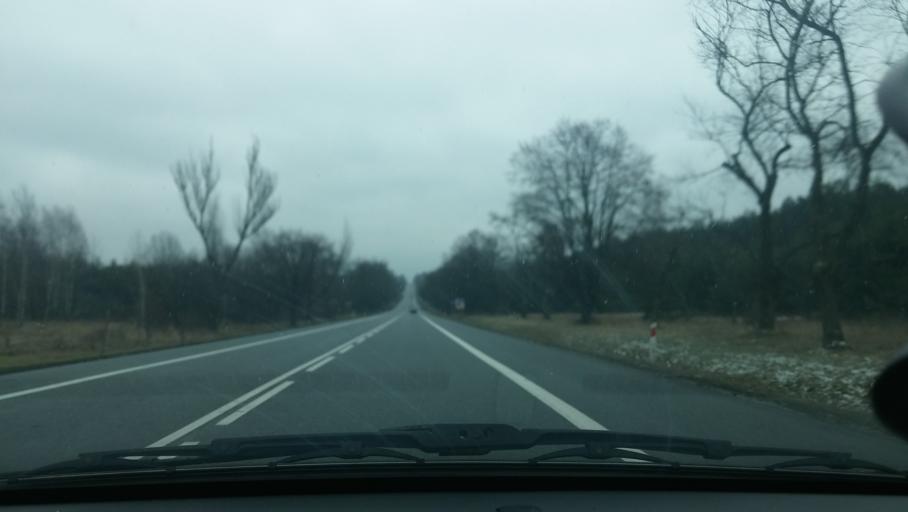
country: PL
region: Masovian Voivodeship
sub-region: Powiat minski
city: Kaluszyn
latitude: 52.2100
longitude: 21.8465
